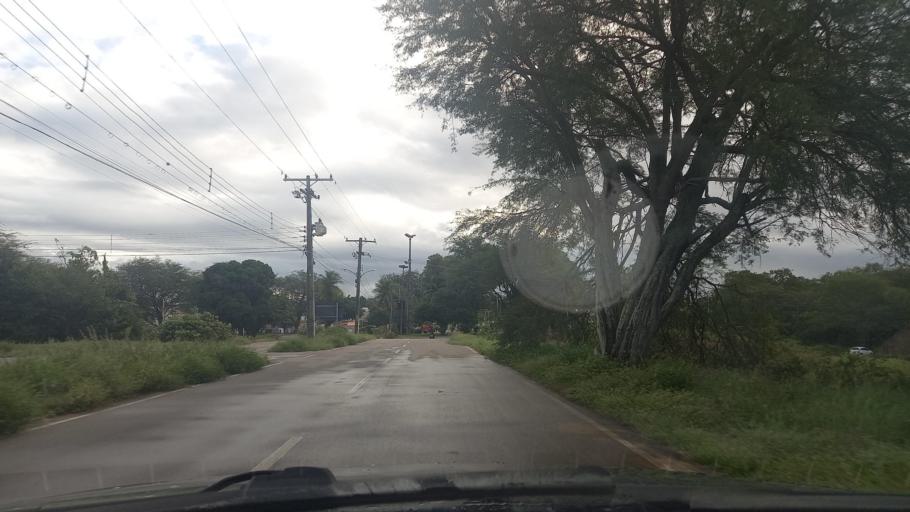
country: BR
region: Bahia
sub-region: Paulo Afonso
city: Paulo Afonso
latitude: -9.3970
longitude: -38.2103
